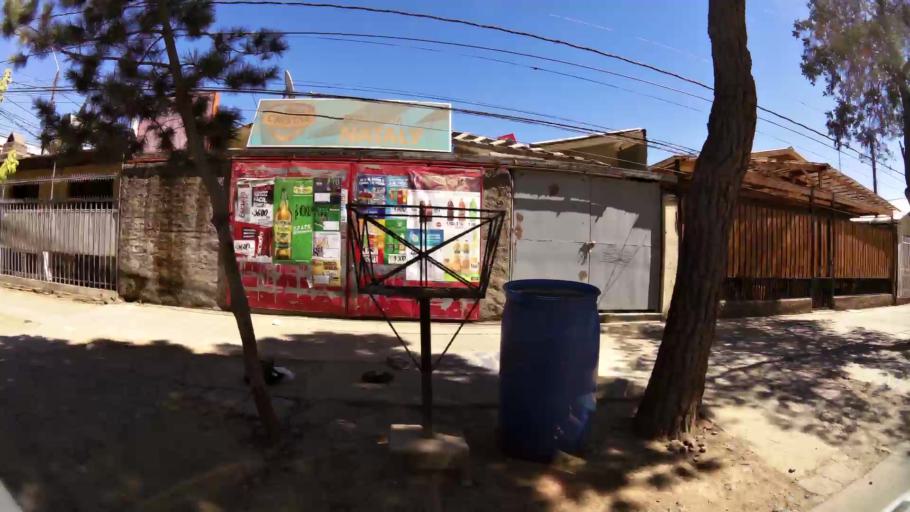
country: CL
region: O'Higgins
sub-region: Provincia de Cachapoal
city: Rancagua
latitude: -34.1666
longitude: -70.7130
